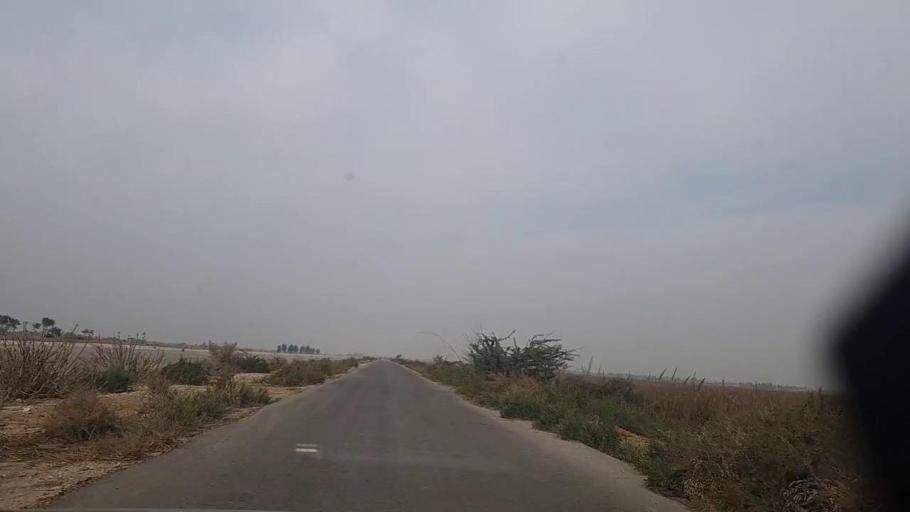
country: PK
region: Sindh
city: Sakrand
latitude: 26.2644
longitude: 68.2400
